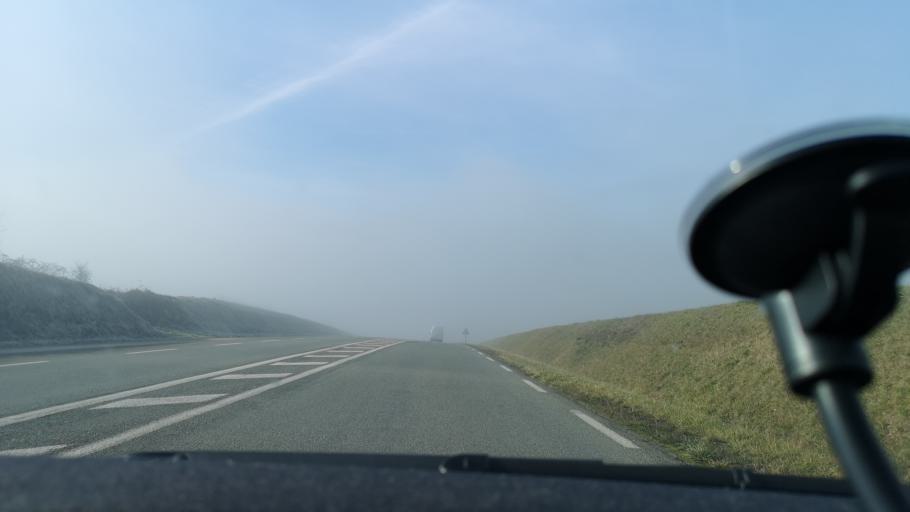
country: FR
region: Franche-Comte
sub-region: Departement du Doubs
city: Clerval
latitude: 47.3821
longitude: 6.4935
